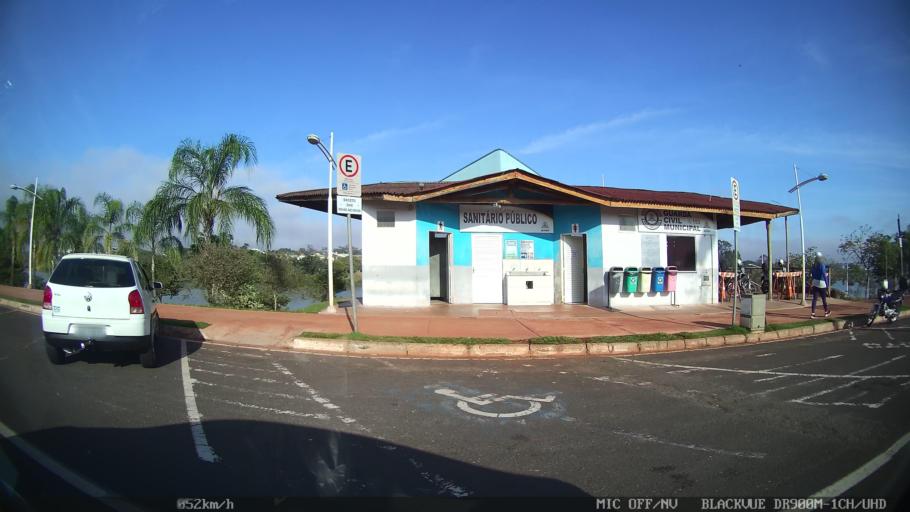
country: BR
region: Sao Paulo
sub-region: Sao Jose Do Rio Preto
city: Sao Jose do Rio Preto
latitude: -20.8140
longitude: -49.3480
